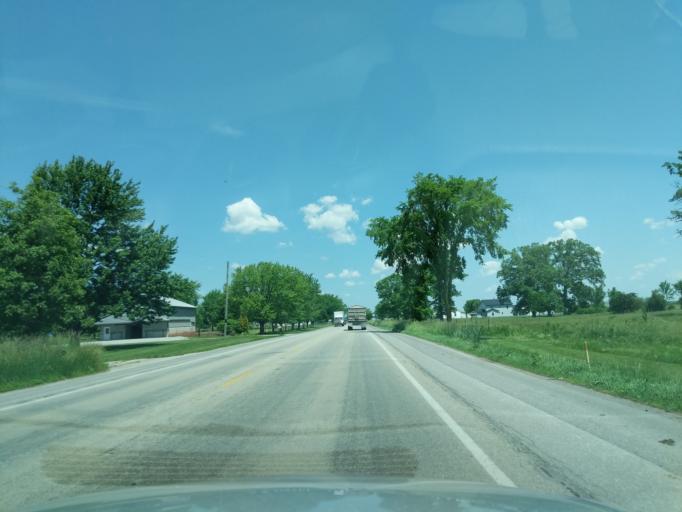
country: US
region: Indiana
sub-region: LaGrange County
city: Topeka
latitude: 41.5699
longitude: -85.5785
